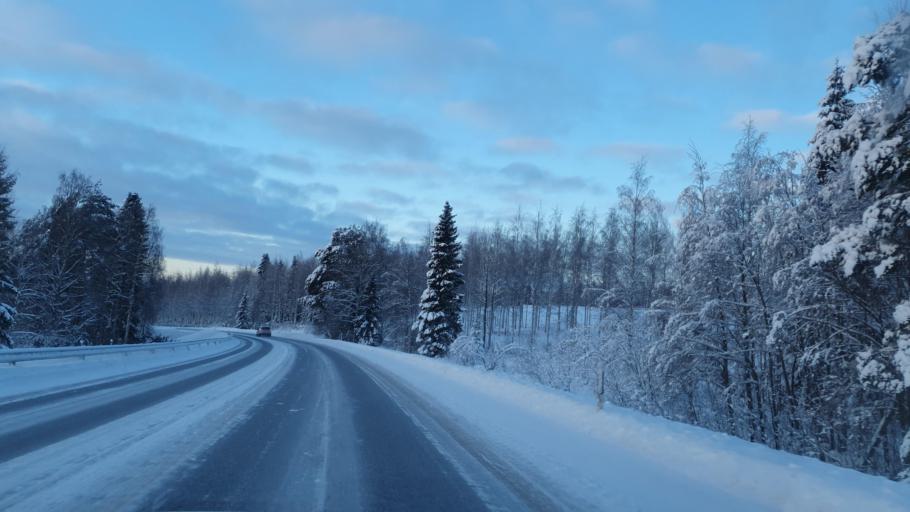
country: FI
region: Kainuu
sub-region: Kajaani
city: Paltamo
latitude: 64.3921
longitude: 27.9790
